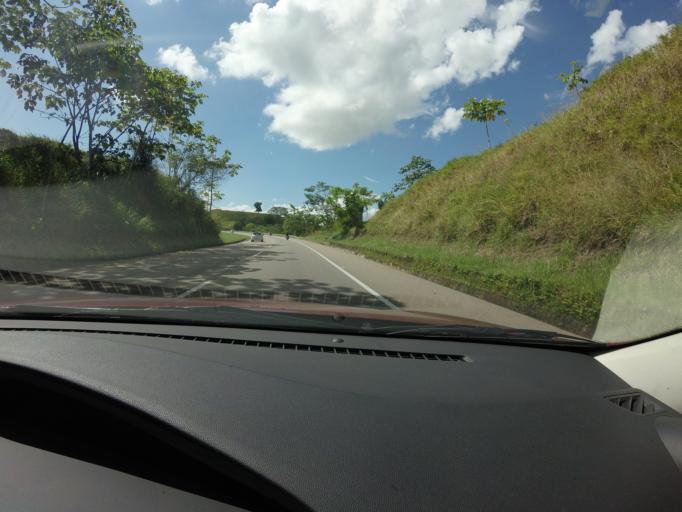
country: CO
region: Antioquia
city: Puerto Triunfo
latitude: 5.7689
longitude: -74.6241
